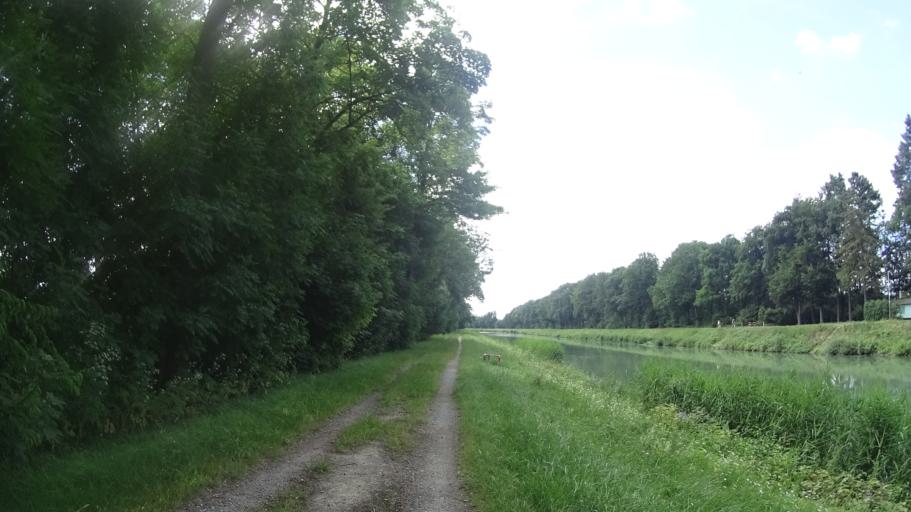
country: DE
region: Lower Saxony
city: Algermissen
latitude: 52.2359
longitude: 9.9447
